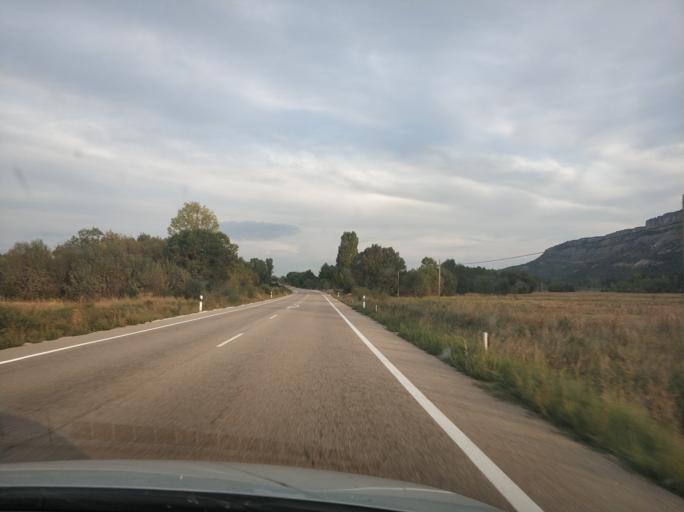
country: ES
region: Castille and Leon
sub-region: Provincia de Burgos
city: Cascajares de la Sierra
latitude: 42.0570
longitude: -3.3916
